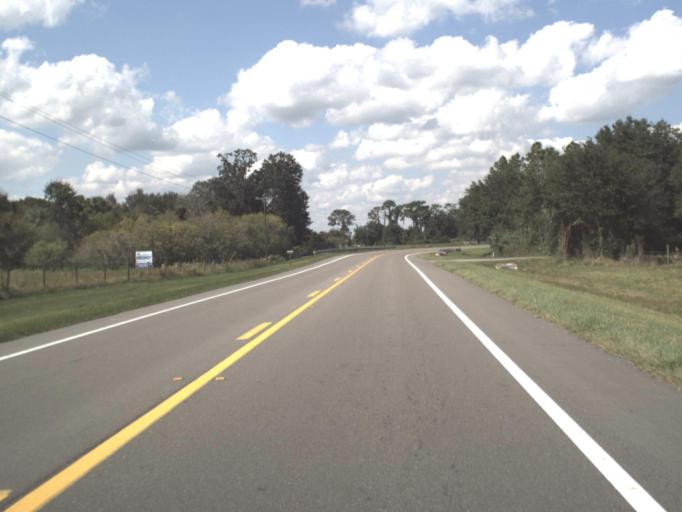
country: US
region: Florida
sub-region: Hardee County
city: Zolfo Springs
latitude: 27.4626
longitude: -81.6982
